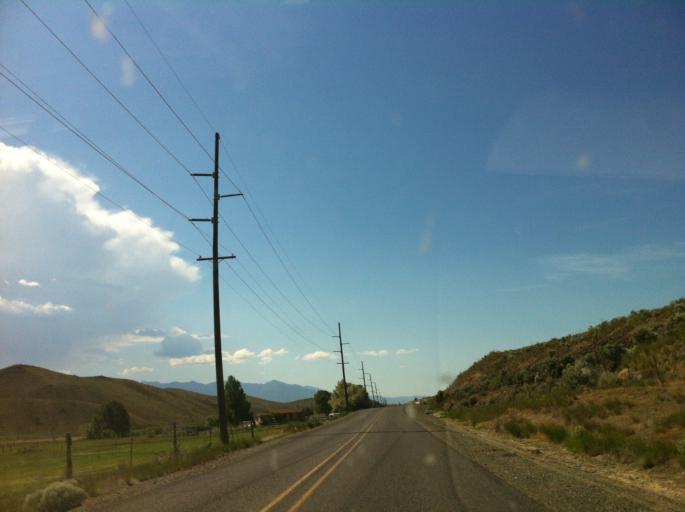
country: US
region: Oregon
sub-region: Baker County
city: Baker City
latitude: 44.7147
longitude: -117.7739
